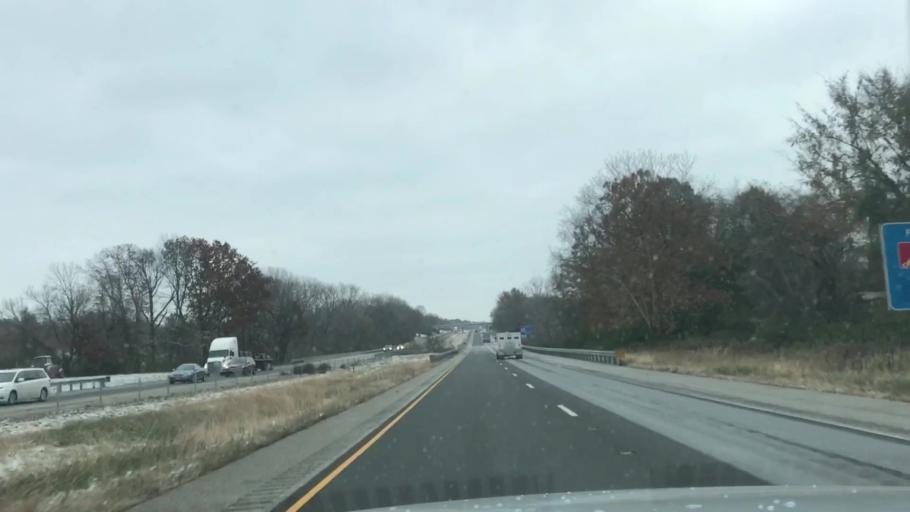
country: US
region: Illinois
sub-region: Madison County
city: Glen Carbon
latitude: 38.7567
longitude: -89.9832
